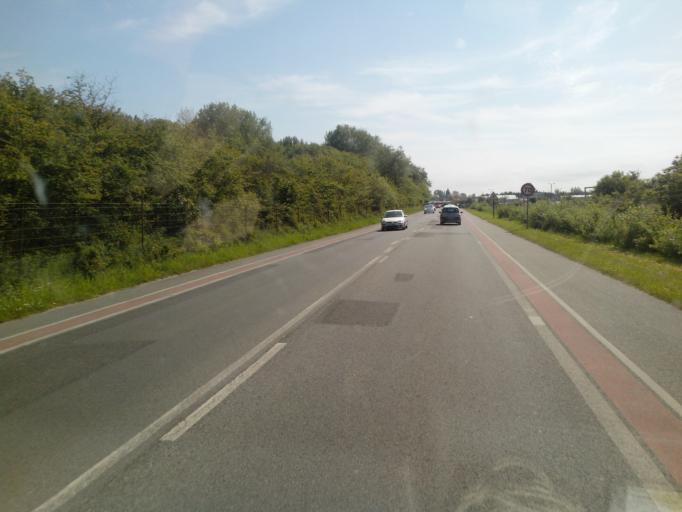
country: FR
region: Nord-Pas-de-Calais
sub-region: Departement du Pas-de-Calais
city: Berck
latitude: 50.4201
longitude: 1.5970
